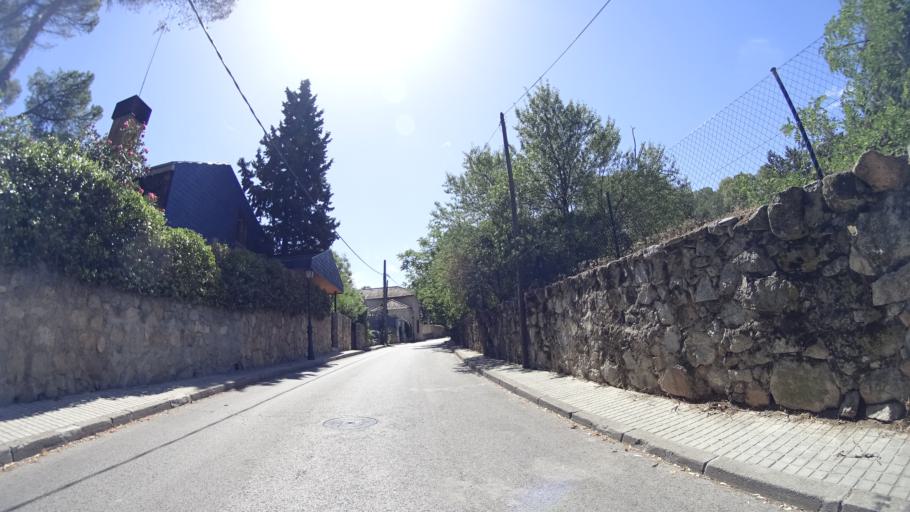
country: ES
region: Madrid
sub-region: Provincia de Madrid
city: Torrelodones
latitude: 40.5729
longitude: -3.9536
